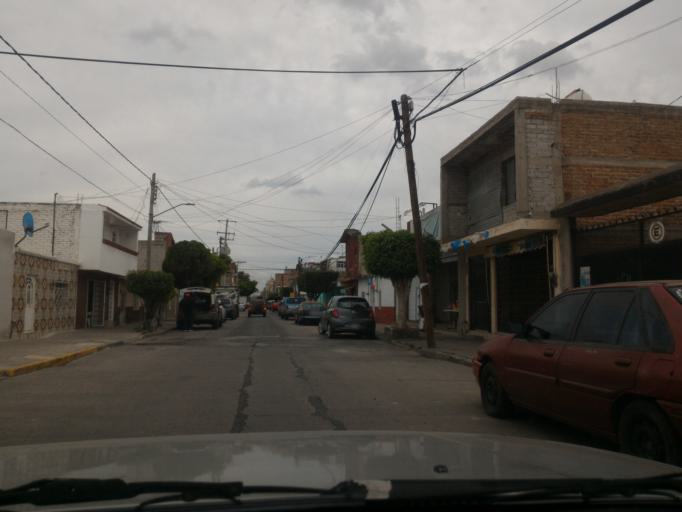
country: MX
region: Guanajuato
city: San Francisco del Rincon
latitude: 21.0248
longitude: -101.8614
